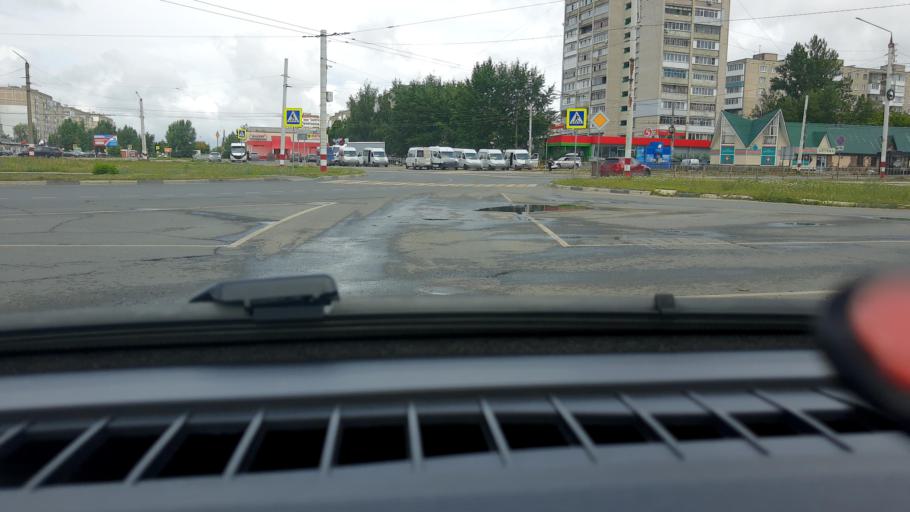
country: RU
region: Nizjnij Novgorod
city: Dzerzhinsk
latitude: 56.2263
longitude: 43.3901
